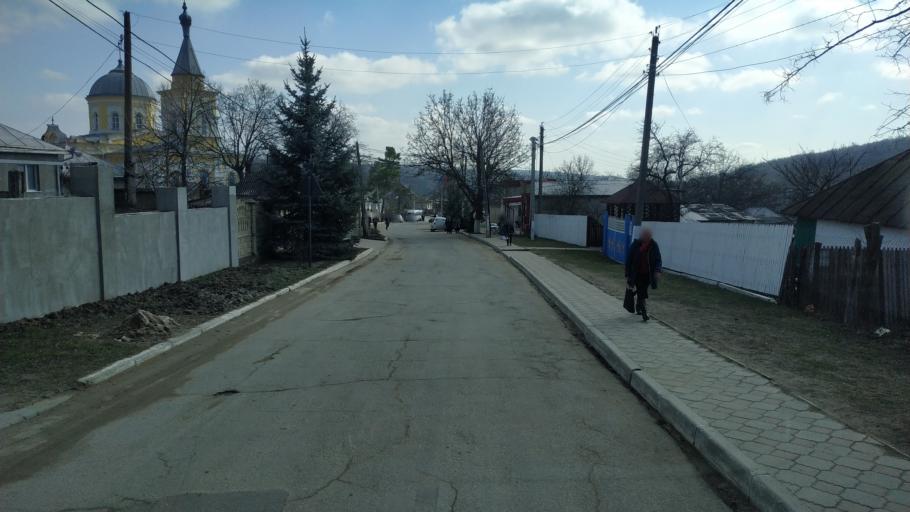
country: MD
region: Hincesti
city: Hincesti
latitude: 46.8254
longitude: 28.6727
